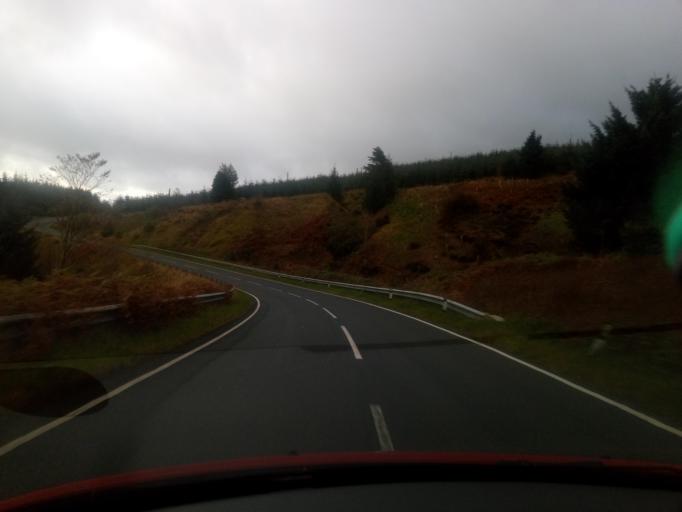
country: GB
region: Scotland
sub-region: The Scottish Borders
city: Hawick
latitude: 55.3119
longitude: -2.6561
